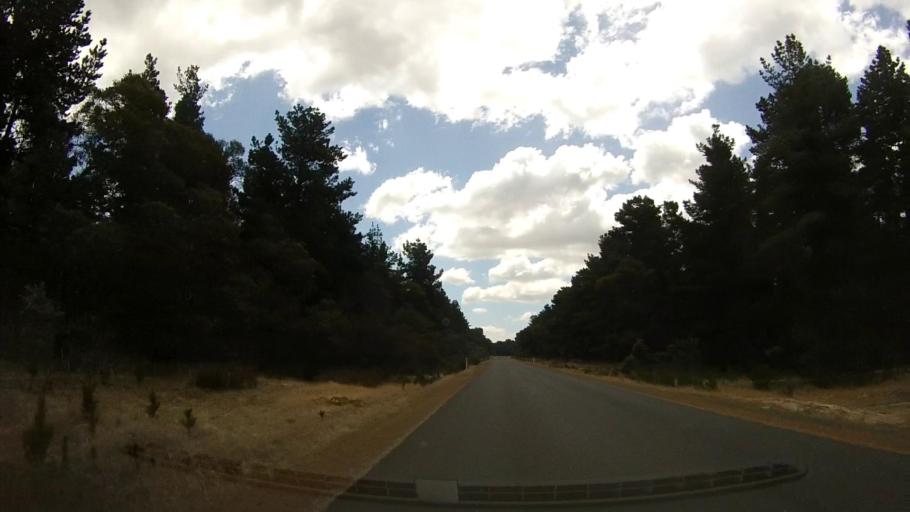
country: AU
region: Tasmania
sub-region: Clarence
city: Seven Mile Beach
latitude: -42.8413
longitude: 147.5320
